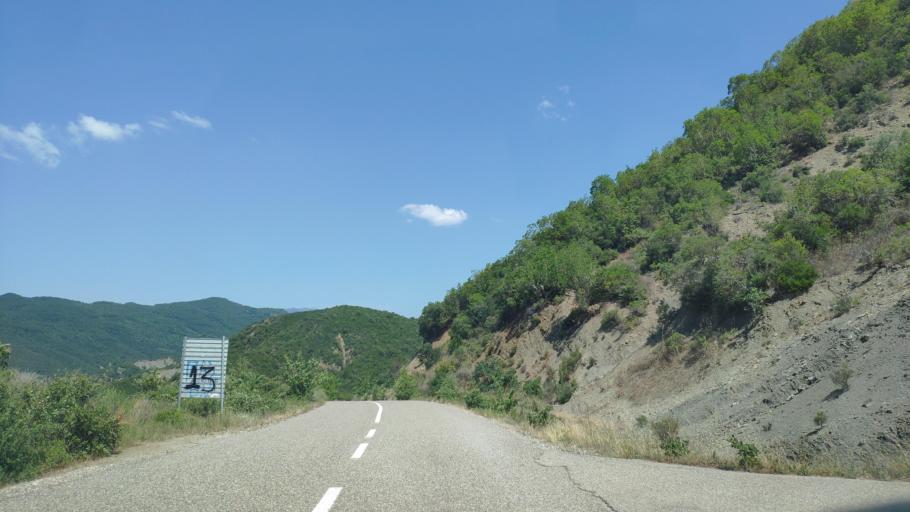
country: GR
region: Central Greece
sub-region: Nomos Evrytanias
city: Kerasochori
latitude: 39.0047
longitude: 21.5368
